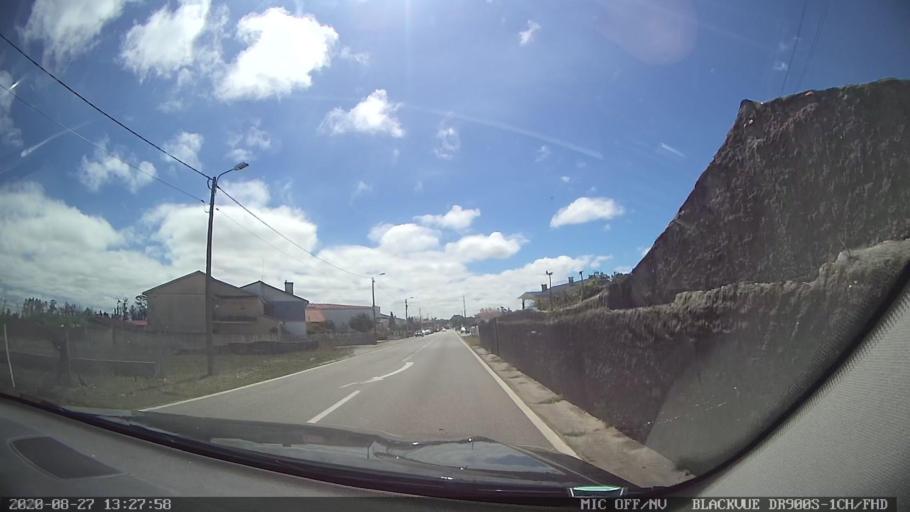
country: PT
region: Aveiro
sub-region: Vagos
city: Vagos
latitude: 40.5252
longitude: -8.6792
